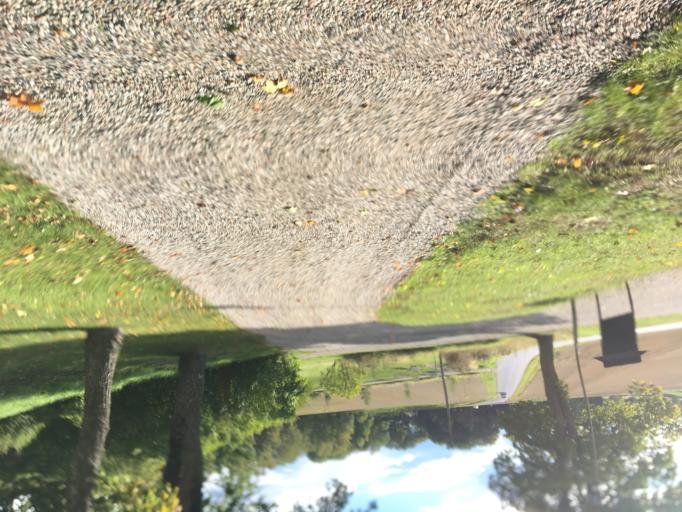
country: SE
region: Soedermanland
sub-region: Eskilstuna Kommun
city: Eskilstuna
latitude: 59.4337
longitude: 16.6341
